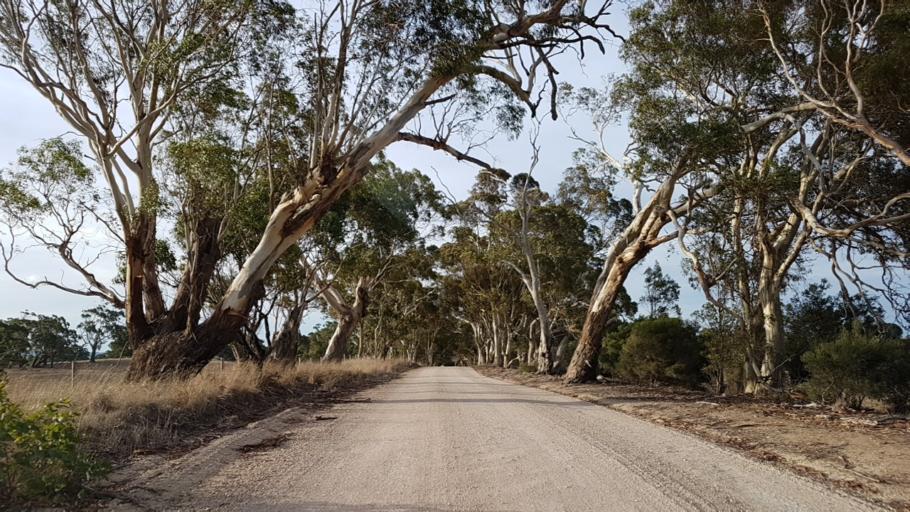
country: AU
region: South Australia
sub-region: Mount Barker
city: Nairne
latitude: -35.0131
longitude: 138.9105
